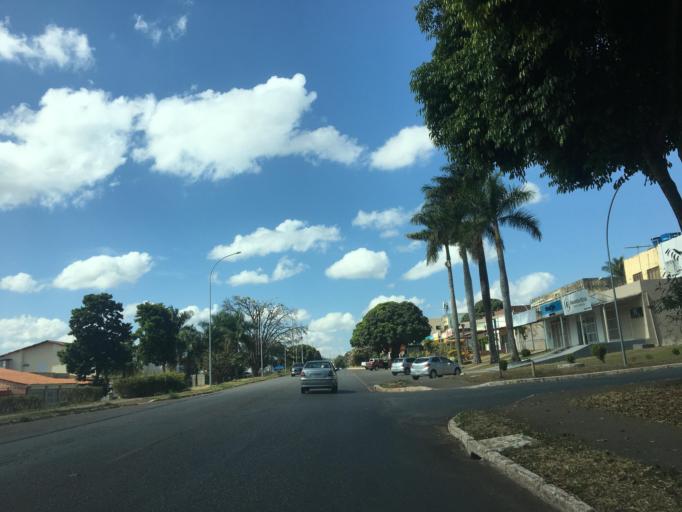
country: BR
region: Federal District
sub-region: Brasilia
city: Brasilia
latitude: -15.6456
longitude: -47.7905
